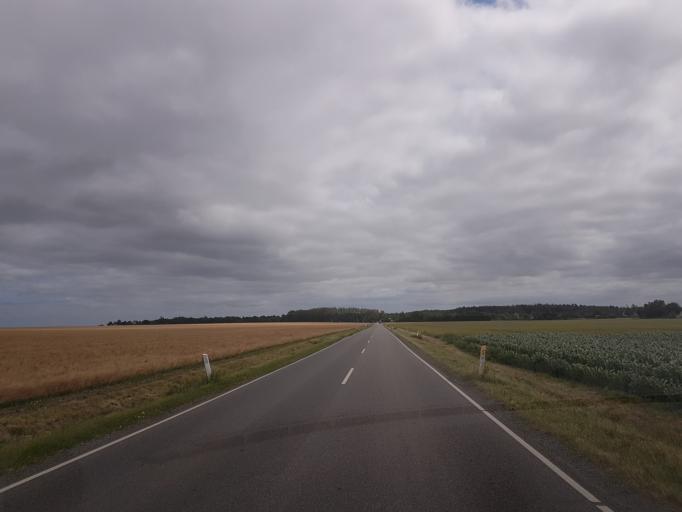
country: DK
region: South Denmark
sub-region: Nordfyns Kommune
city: Bogense
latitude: 55.5680
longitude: 10.1754
